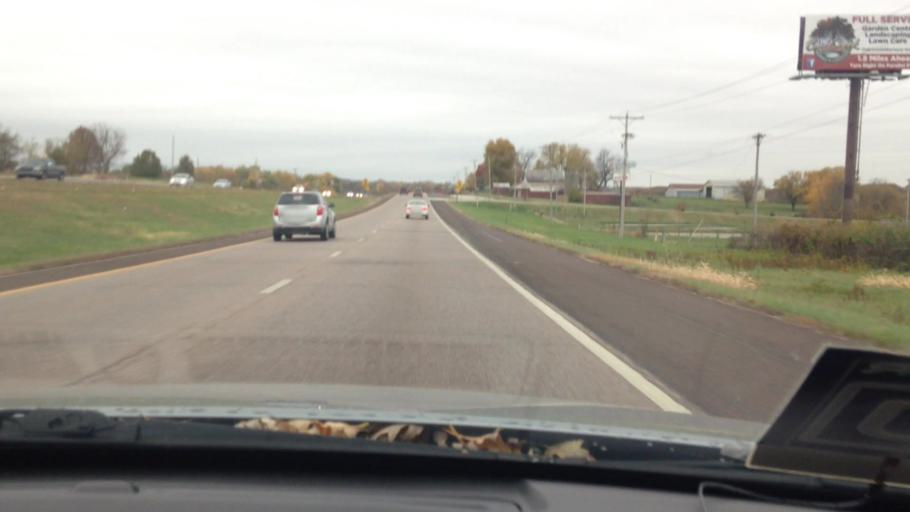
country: US
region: Kansas
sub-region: Leavenworth County
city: Basehor
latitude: 39.1529
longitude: -94.8999
